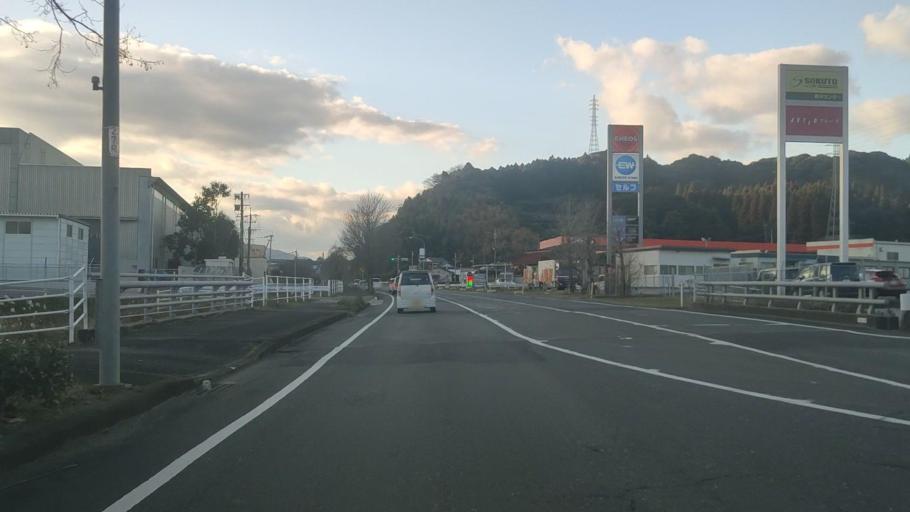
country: JP
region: Saga Prefecture
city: Takeocho-takeo
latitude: 33.2890
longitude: 130.1318
